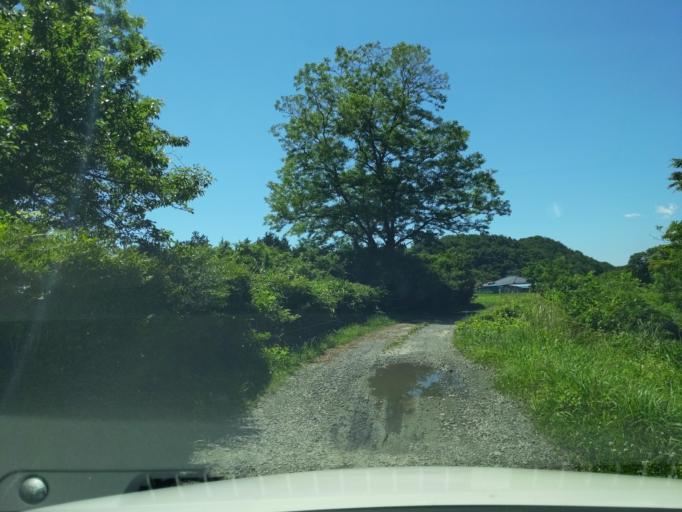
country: JP
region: Fukushima
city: Koriyama
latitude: 37.3903
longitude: 140.2617
